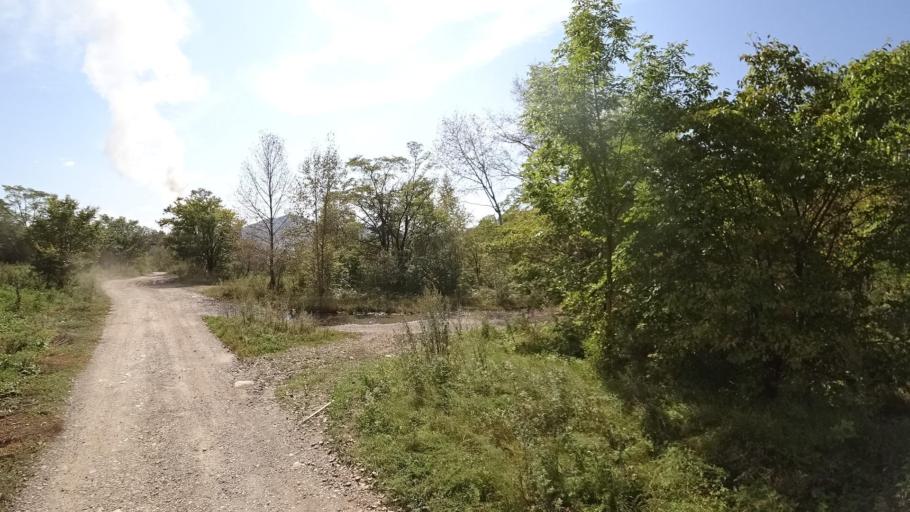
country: RU
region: Jewish Autonomous Oblast
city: Londoko
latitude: 49.0121
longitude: 131.8968
